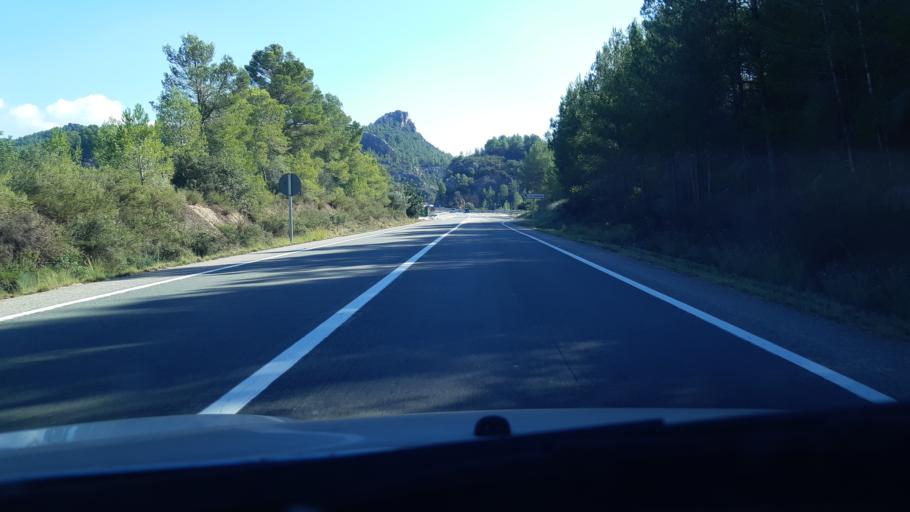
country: ES
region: Catalonia
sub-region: Provincia de Tarragona
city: Benifallet
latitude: 40.9441
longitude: 0.4852
